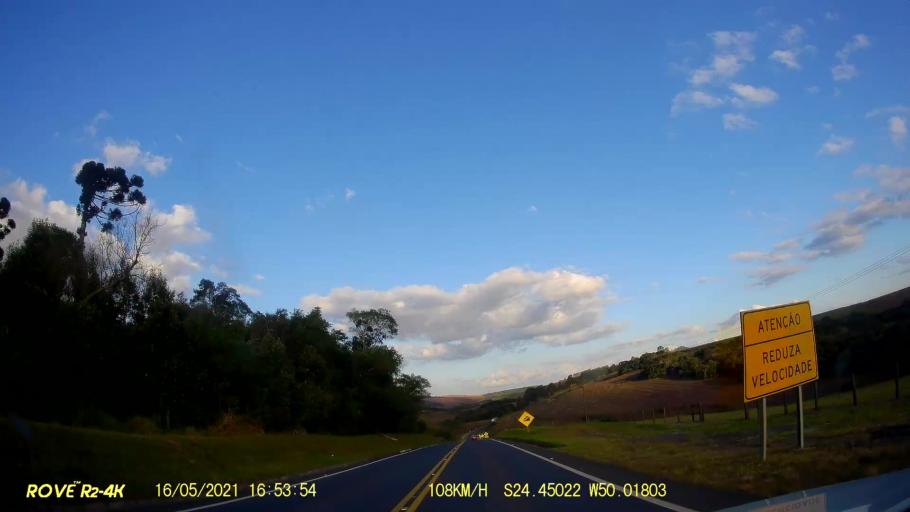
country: BR
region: Parana
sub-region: Pirai Do Sul
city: Pirai do Sul
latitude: -24.4504
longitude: -50.0176
